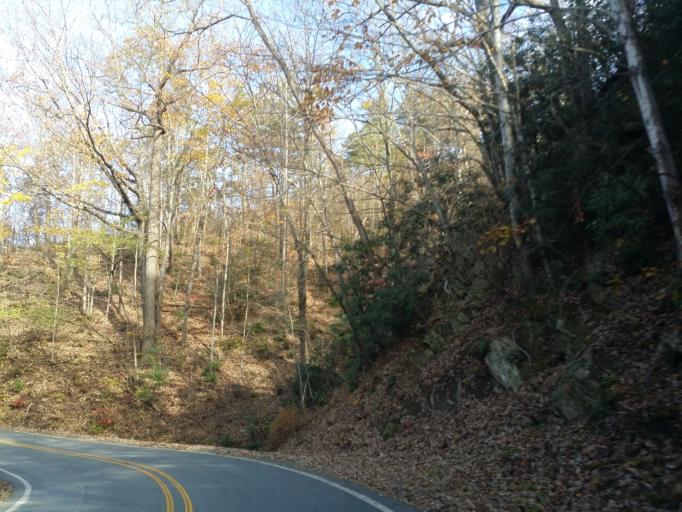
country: US
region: North Carolina
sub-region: McDowell County
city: West Marion
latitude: 35.7526
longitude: -82.1526
